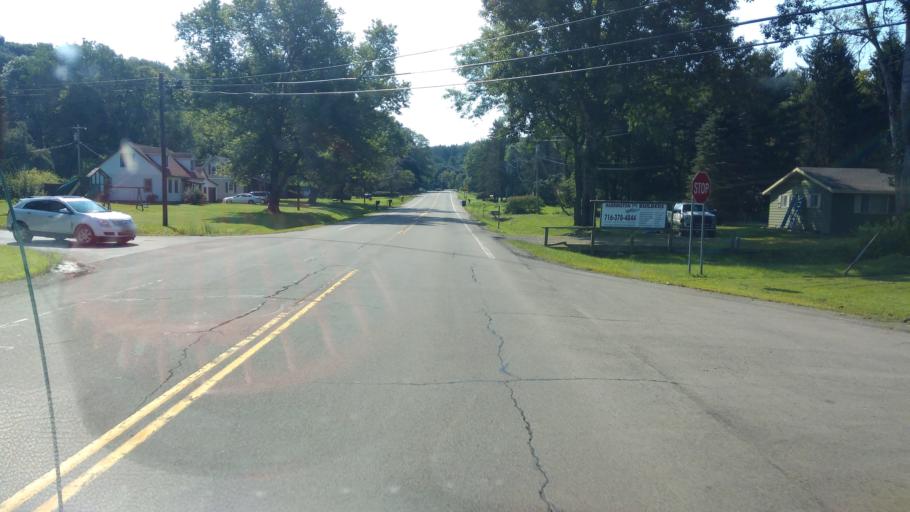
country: US
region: New York
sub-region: Allegany County
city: Cuba
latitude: 42.1998
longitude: -78.2735
